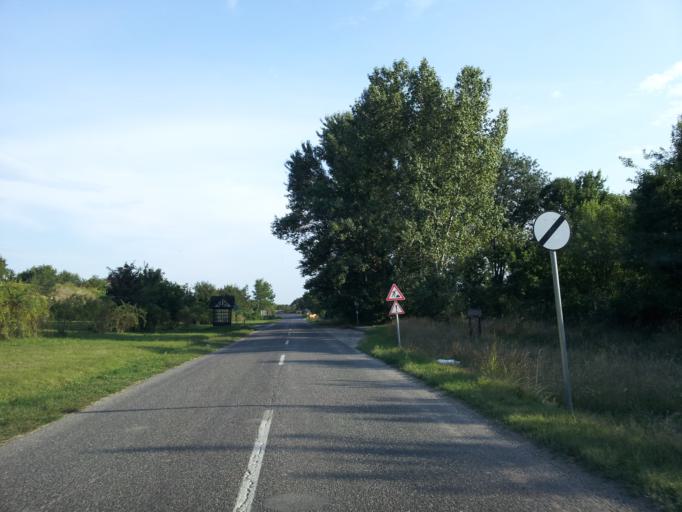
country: HU
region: Somogy
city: Zamardi
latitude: 46.8652
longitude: 18.0108
